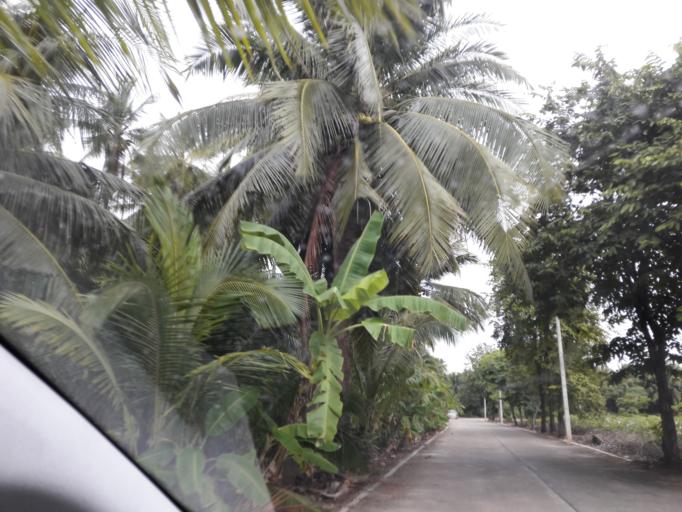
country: TH
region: Ratchaburi
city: Damnoen Saduak
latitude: 13.5206
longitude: 99.9566
